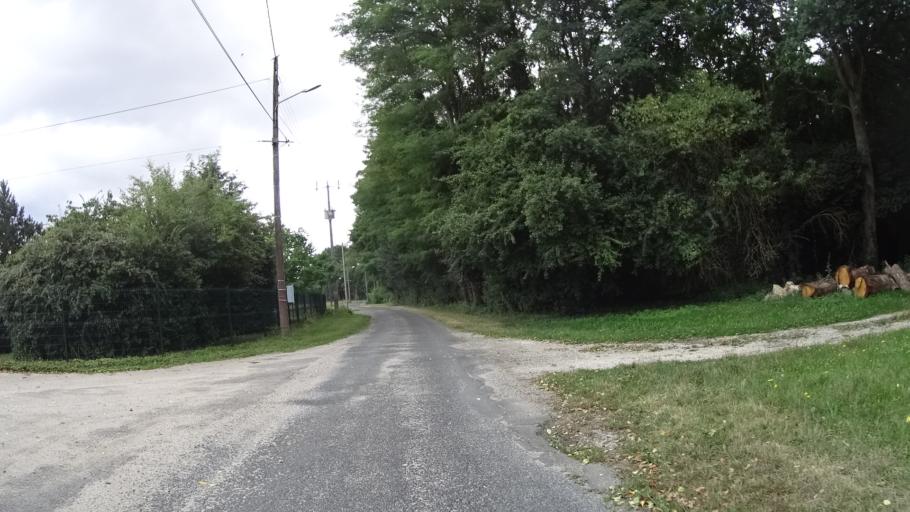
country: FR
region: Centre
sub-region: Departement du Loiret
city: Pannes
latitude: 47.9855
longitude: 2.6792
